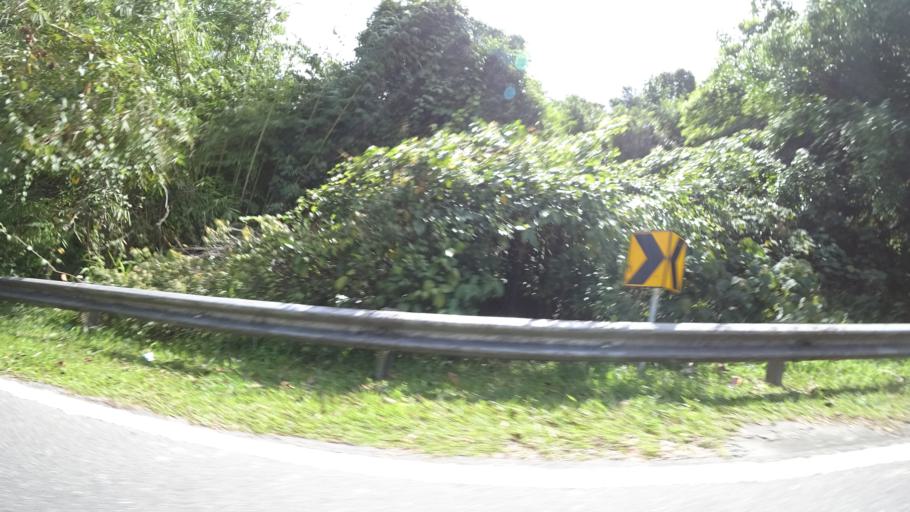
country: BN
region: Brunei and Muara
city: Bandar Seri Begawan
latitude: 4.8823
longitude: 114.9634
